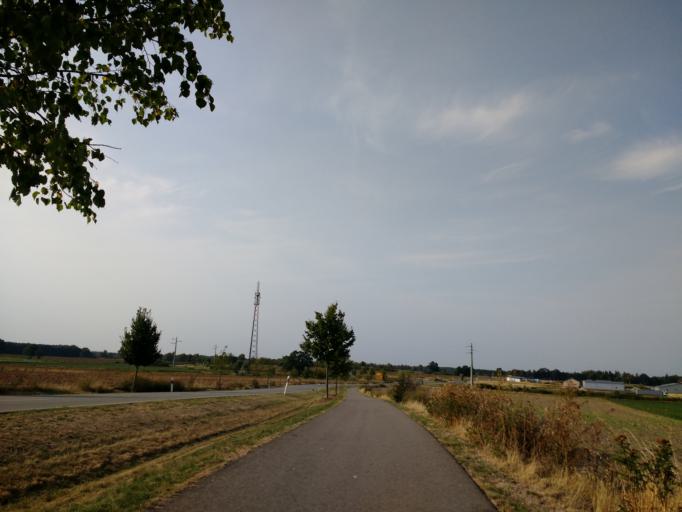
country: DE
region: Lower Saxony
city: Gifhorn
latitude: 52.5026
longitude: 10.5310
